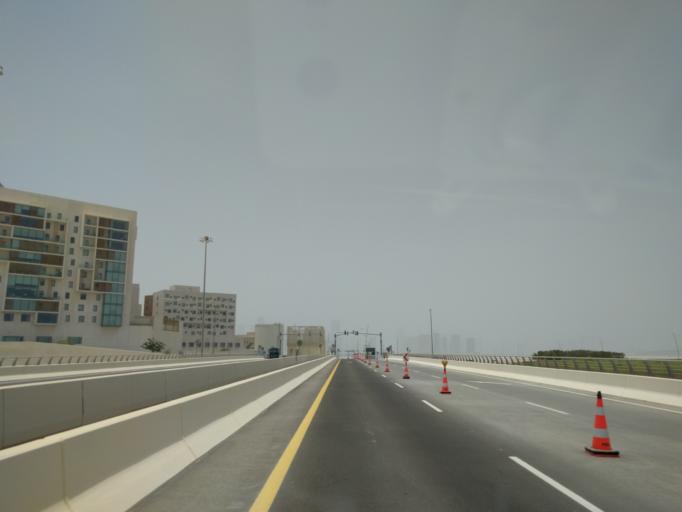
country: AE
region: Abu Dhabi
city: Abu Dhabi
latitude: 24.5272
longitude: 54.4337
